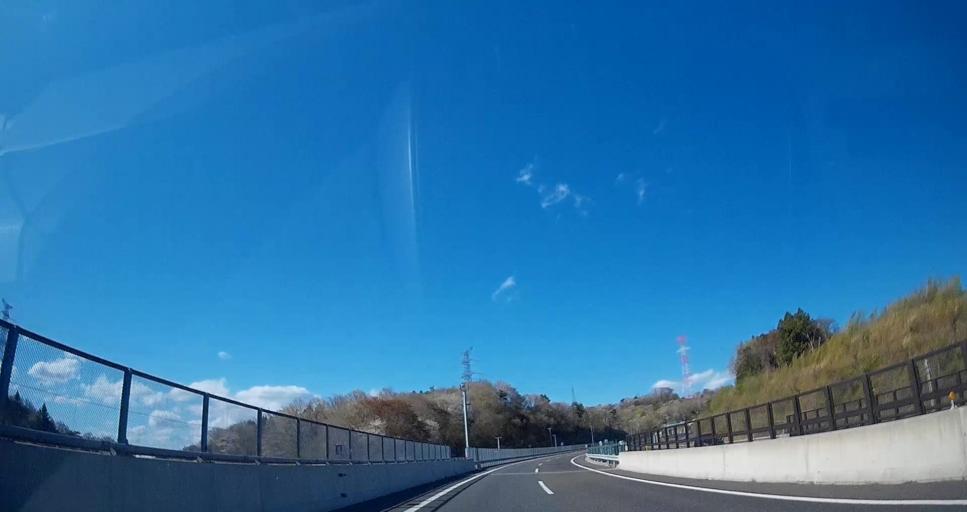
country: JP
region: Miyagi
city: Matsushima
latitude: 38.4011
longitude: 141.0407
